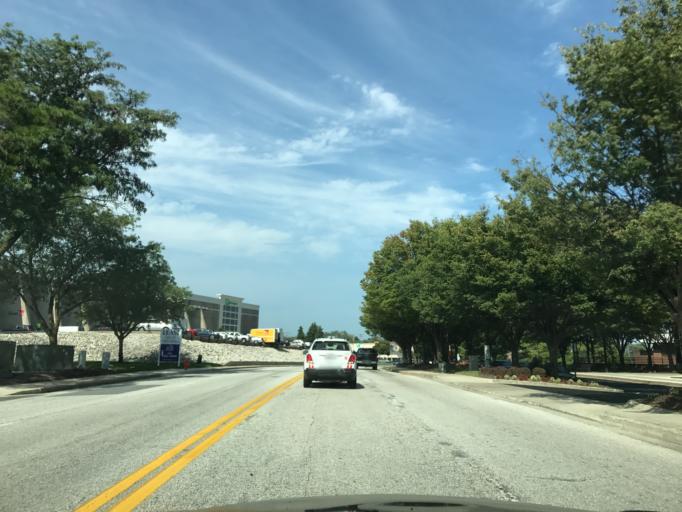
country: US
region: Maryland
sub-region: Baltimore County
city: Mays Chapel
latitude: 39.4535
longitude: -76.6400
